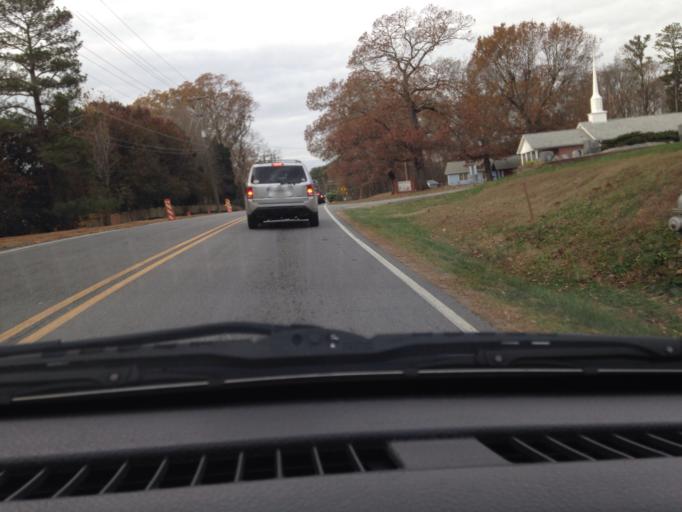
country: US
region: Georgia
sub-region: Fulton County
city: Johns Creek
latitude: 34.0838
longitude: -84.1875
